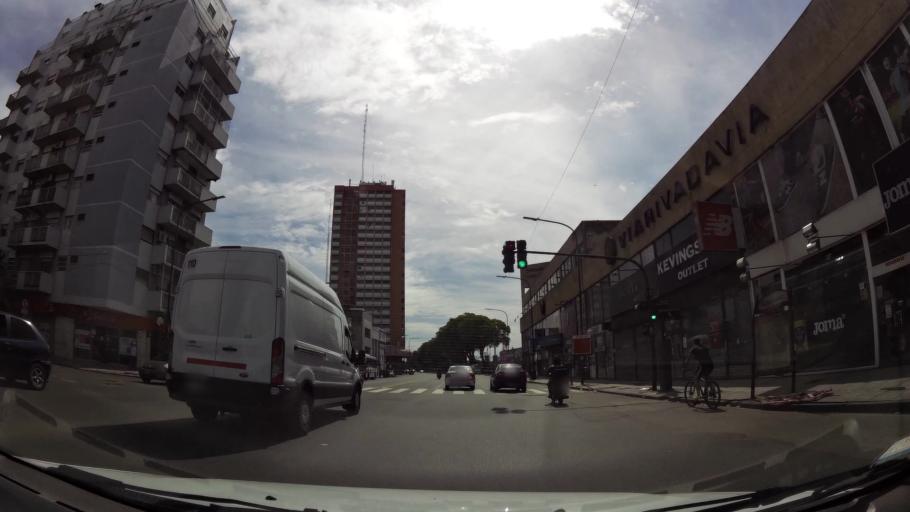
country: AR
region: Buenos Aires F.D.
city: Villa Santa Rita
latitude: -34.6389
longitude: -58.5212
